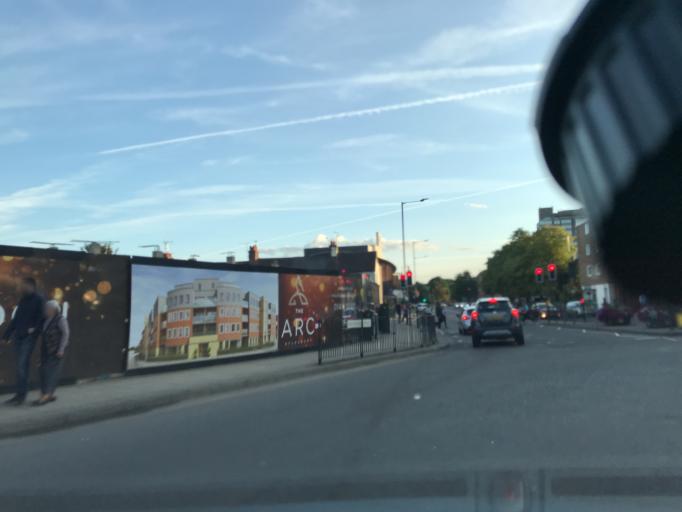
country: GB
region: England
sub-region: Buckinghamshire
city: Aylesbury
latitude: 51.8167
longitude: -0.8080
